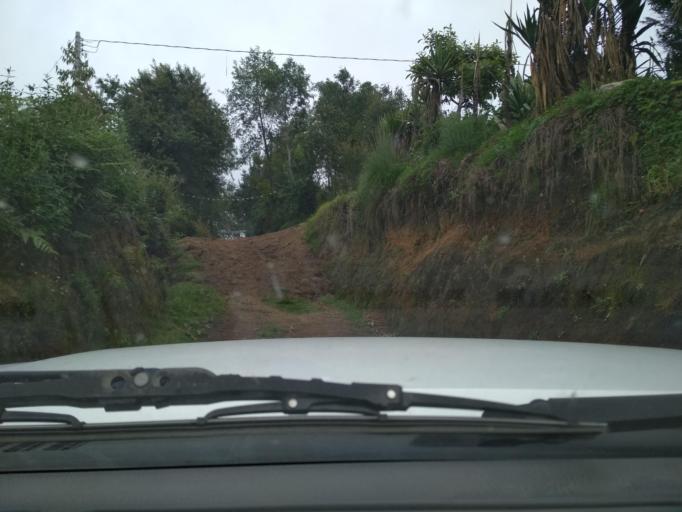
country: MX
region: Veracruz
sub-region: La Perla
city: Chilapa
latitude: 18.9914
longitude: -97.1671
